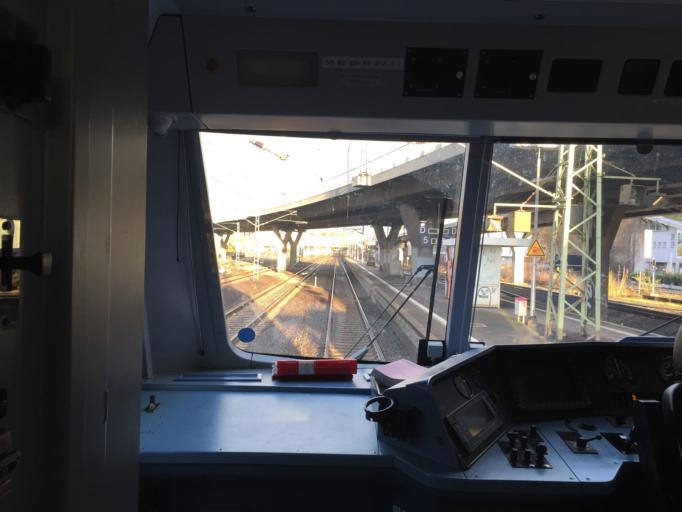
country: DE
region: Hesse
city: Niederrad
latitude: 50.1201
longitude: 8.6377
